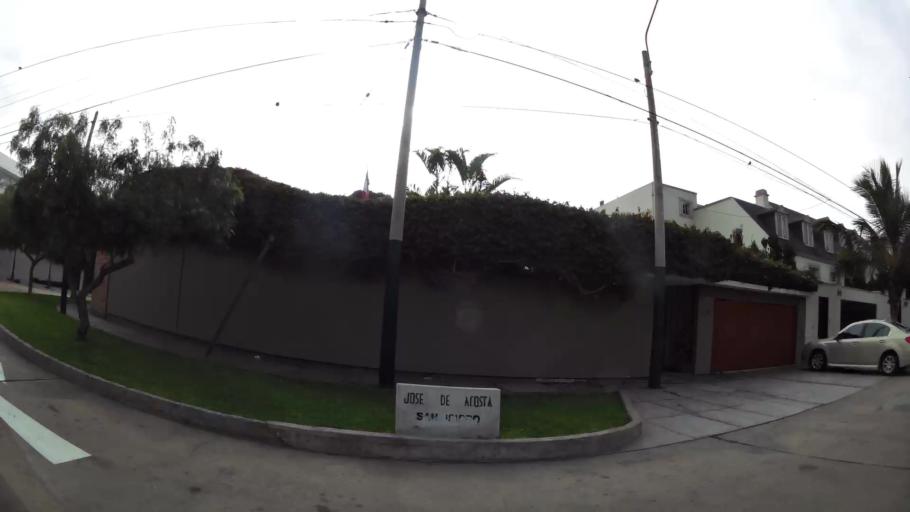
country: PE
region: Lima
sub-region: Lima
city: San Isidro
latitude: -12.0995
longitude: -77.0590
